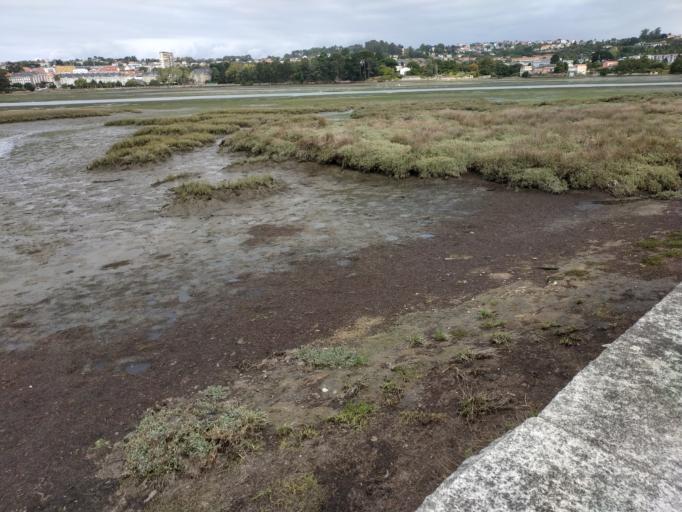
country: ES
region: Galicia
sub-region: Provincia da Coruna
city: Culleredo
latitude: 43.3226
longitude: -8.3747
